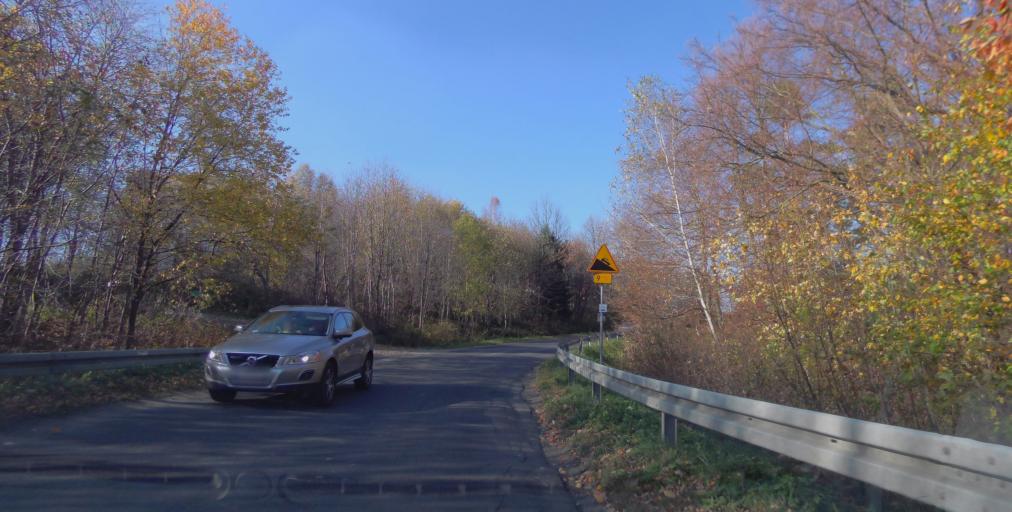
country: PL
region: Subcarpathian Voivodeship
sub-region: Powiat leski
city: Polanczyk
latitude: 49.3440
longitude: 22.4126
